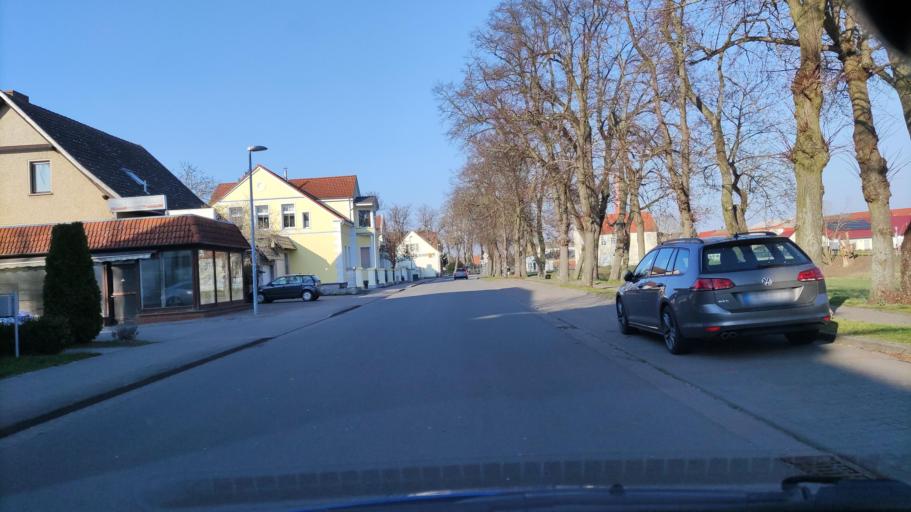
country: DE
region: Saxony-Anhalt
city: Seehausen
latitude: 52.8902
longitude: 11.7495
